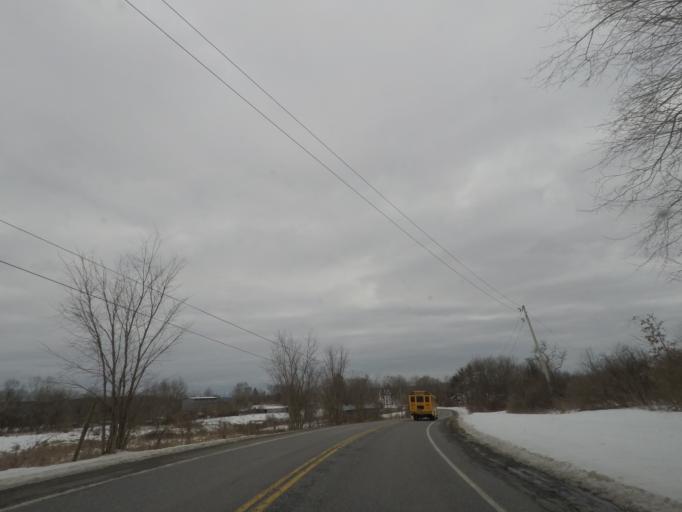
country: US
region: New York
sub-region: Saratoga County
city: Stillwater
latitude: 42.9459
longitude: -73.6628
